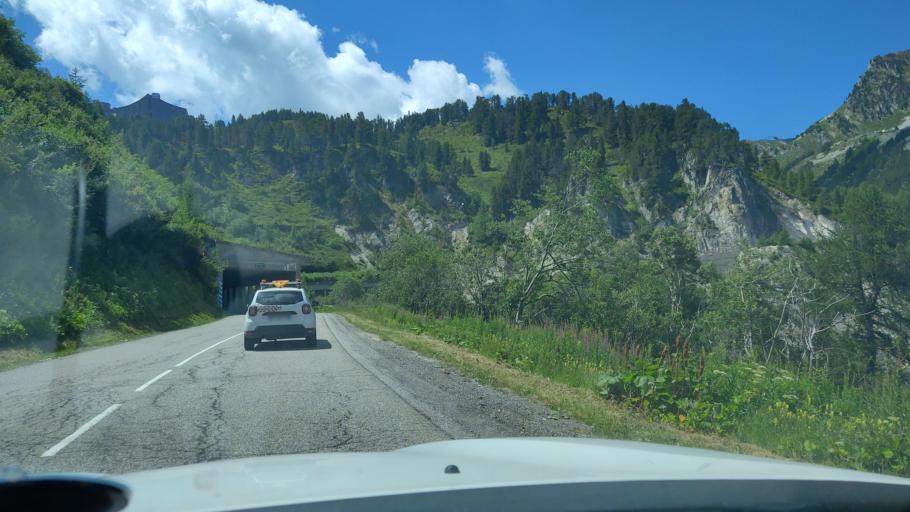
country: FR
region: Rhone-Alpes
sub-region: Departement de la Savoie
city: Seez
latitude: 45.5793
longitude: 6.8351
